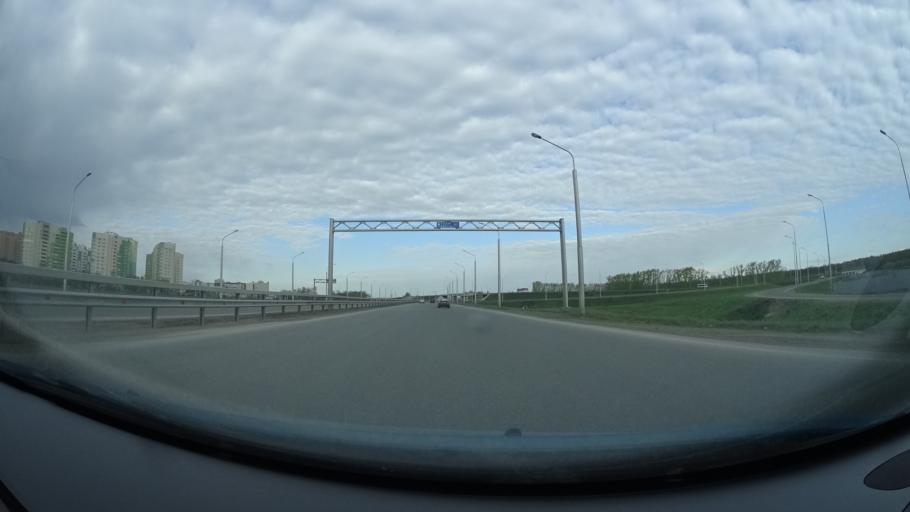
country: RU
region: Bashkortostan
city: Mikhaylovka
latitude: 54.7982
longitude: 55.8733
